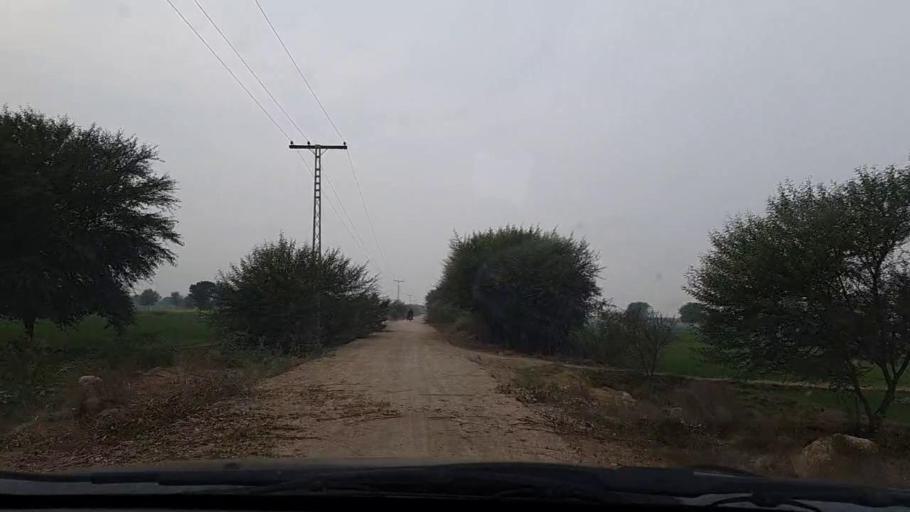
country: PK
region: Sindh
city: Pithoro
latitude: 25.7654
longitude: 69.3846
